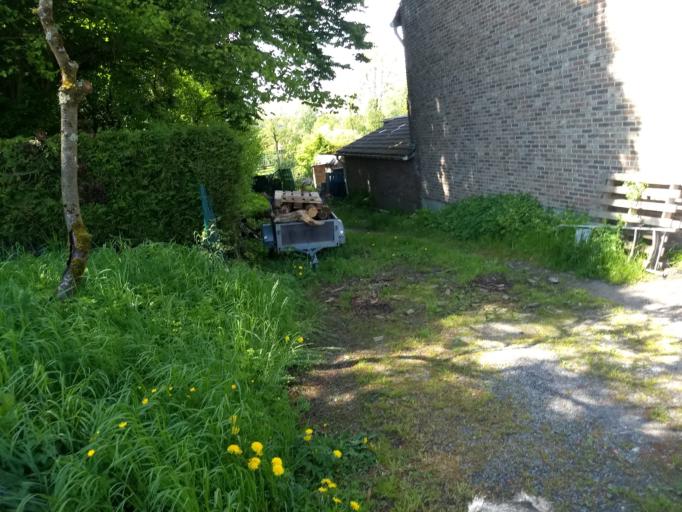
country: BE
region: Flanders
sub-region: Provincie Vlaams-Brabant
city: Beersel
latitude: 50.7310
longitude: 4.3107
